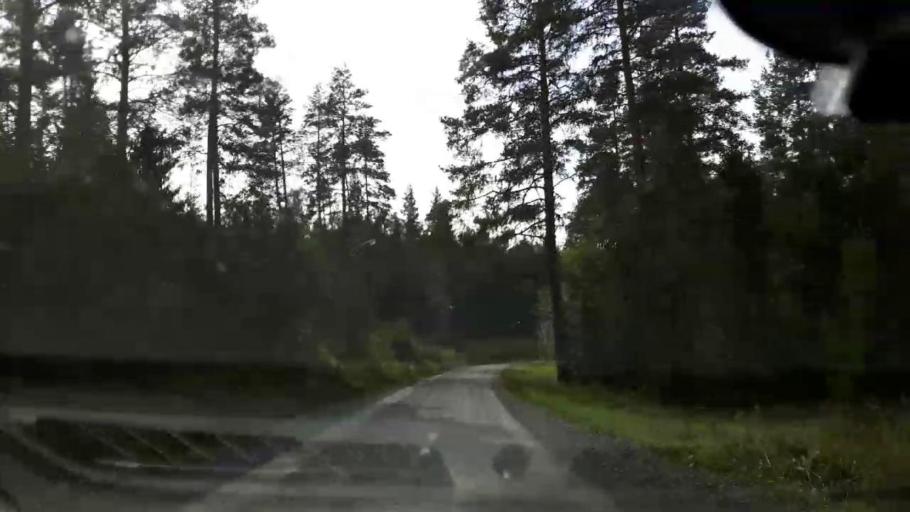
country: SE
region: Jaemtland
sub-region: Ragunda Kommun
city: Hammarstrand
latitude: 63.1403
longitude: 16.2002
